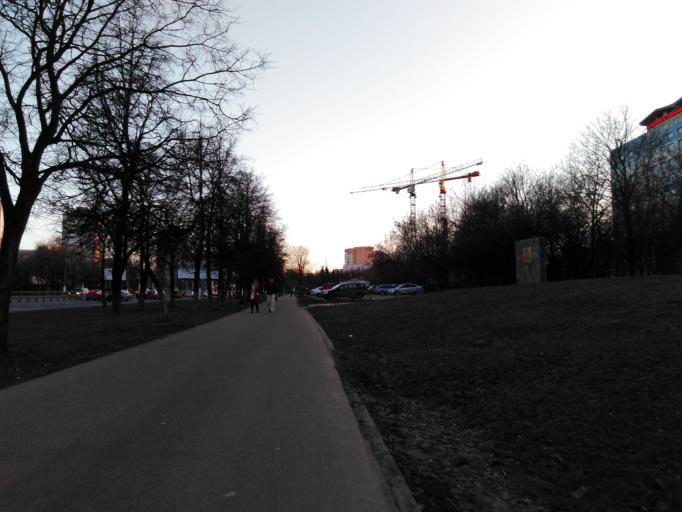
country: RU
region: Moskovskaya
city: Cheremushki
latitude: 55.6528
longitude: 37.5352
